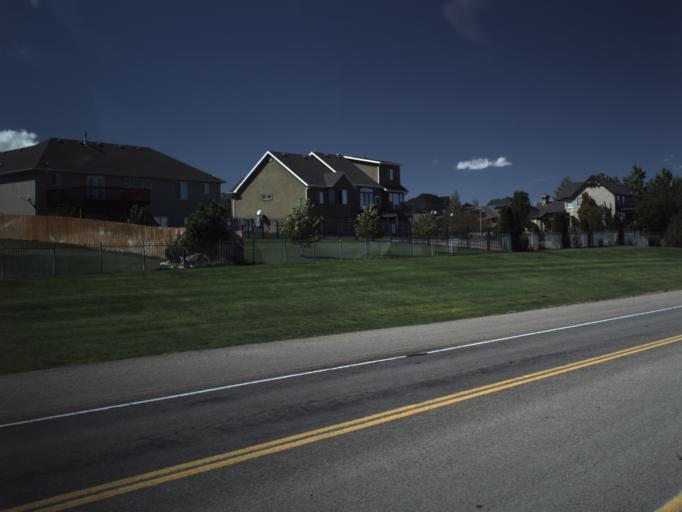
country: US
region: Utah
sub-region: Utah County
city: Saratoga Springs
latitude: 40.3193
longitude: -111.8999
